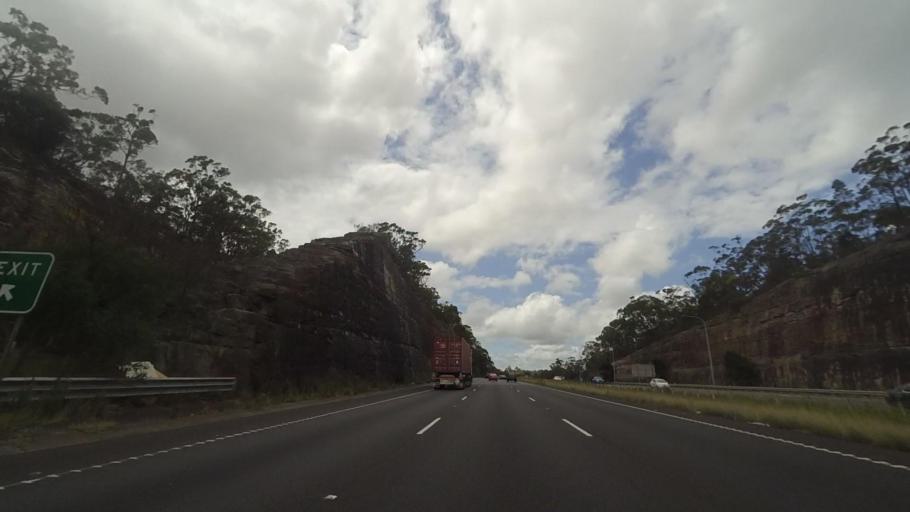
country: AU
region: New South Wales
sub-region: Gosford Shire
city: Point Clare
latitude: -33.4314
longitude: 151.2234
